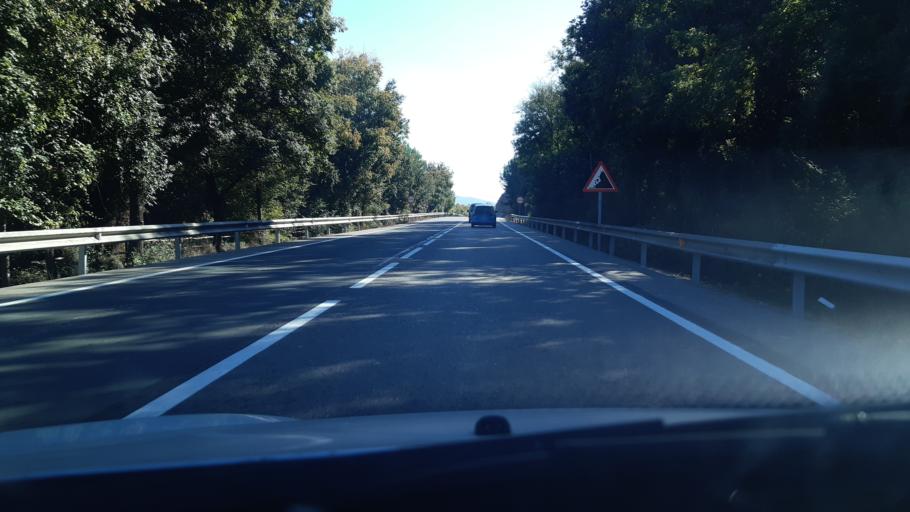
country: ES
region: Catalonia
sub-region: Provincia de Tarragona
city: Tivenys
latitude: 40.8635
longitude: 0.5070
